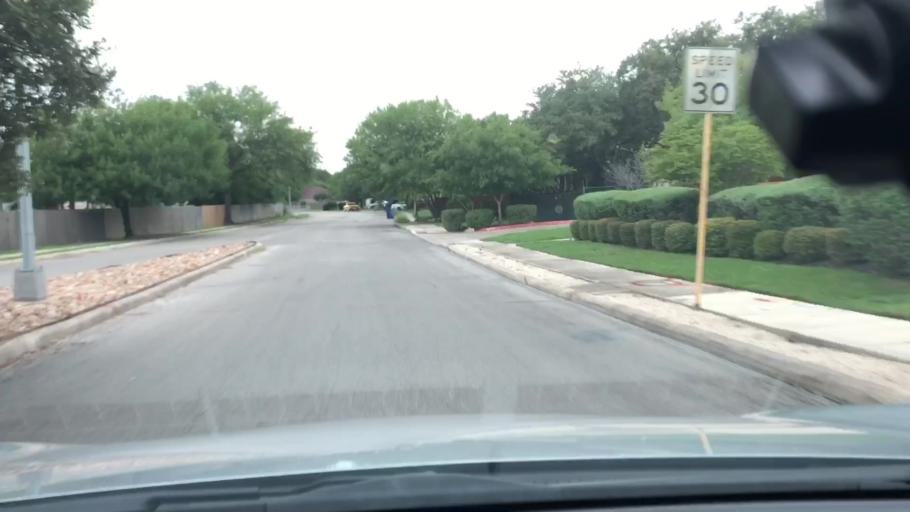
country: US
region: Texas
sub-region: Bexar County
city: Leon Valley
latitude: 29.4997
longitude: -98.6625
